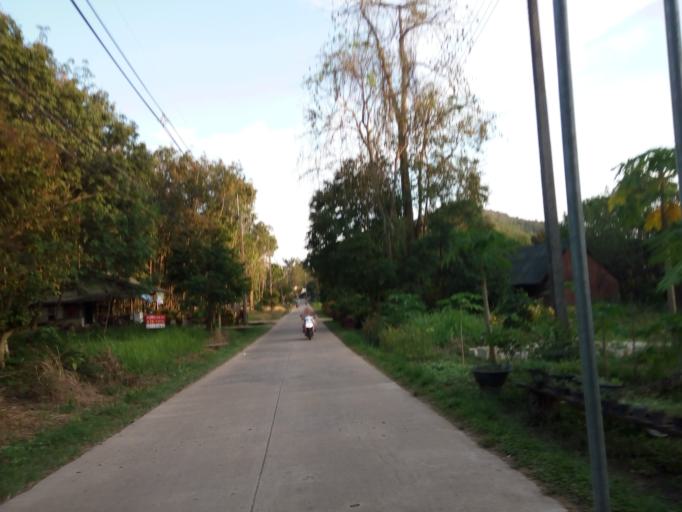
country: TH
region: Phangnga
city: Ko Yao
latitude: 8.0955
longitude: 98.6109
